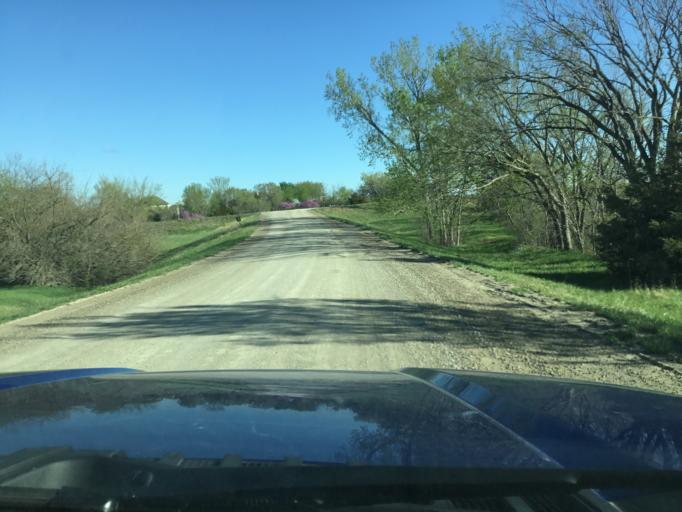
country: US
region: Kansas
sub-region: Douglas County
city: Lawrence
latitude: 38.9701
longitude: -95.3725
